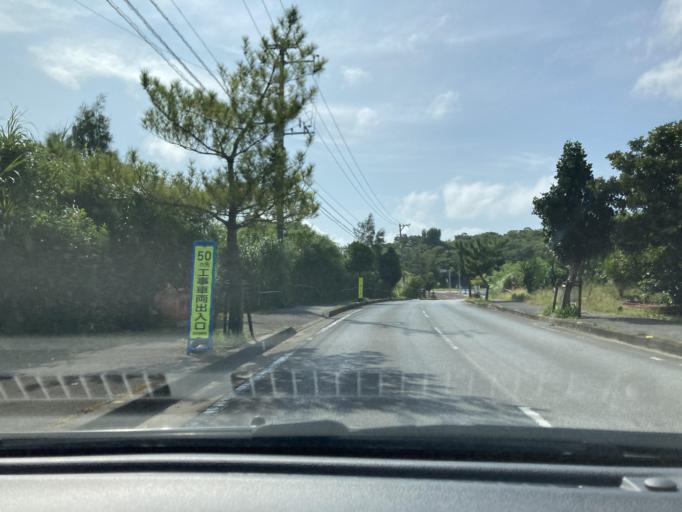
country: JP
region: Okinawa
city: Chatan
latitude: 26.2874
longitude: 127.8037
